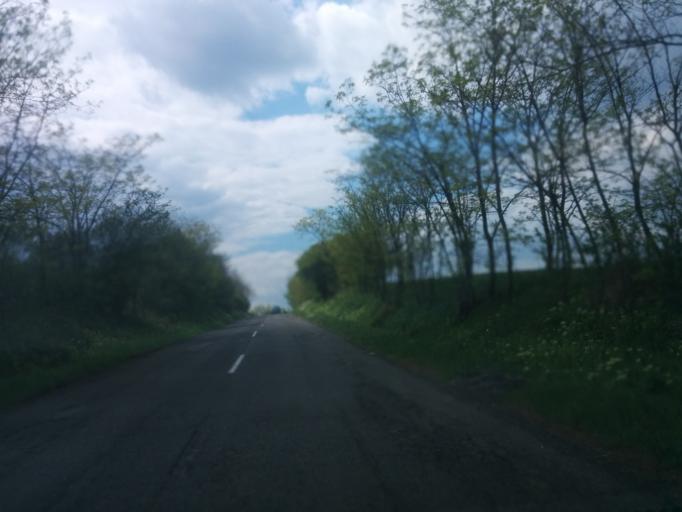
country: HU
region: Nograd
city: Palotas
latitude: 47.8297
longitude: 19.5618
